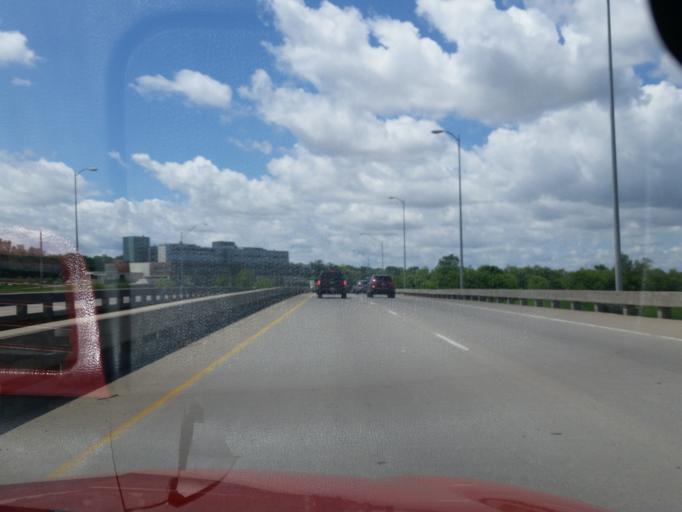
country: US
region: Nebraska
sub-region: Sarpy County
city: Offutt Air Force Base
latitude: 41.1397
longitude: -95.9425
